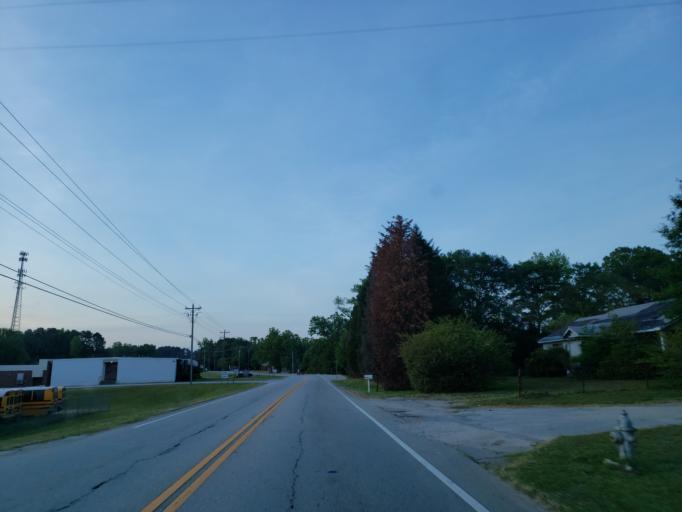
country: US
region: Georgia
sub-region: Douglas County
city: Douglasville
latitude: 33.6723
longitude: -84.8054
